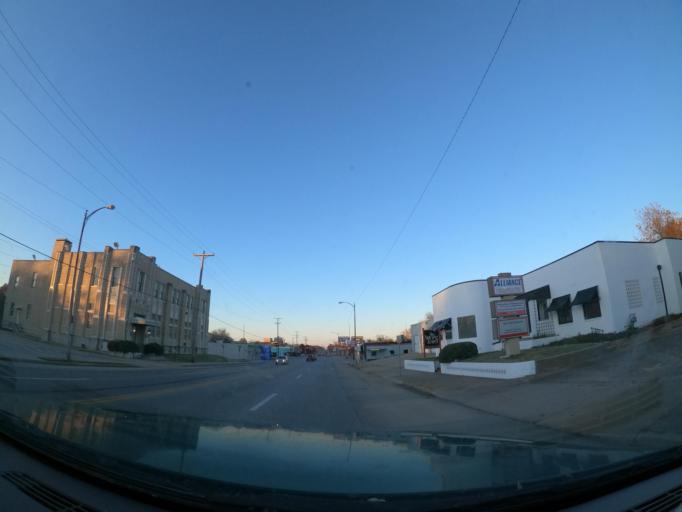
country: US
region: Oklahoma
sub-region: Tulsa County
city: Tulsa
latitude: 36.1454
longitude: -95.9403
